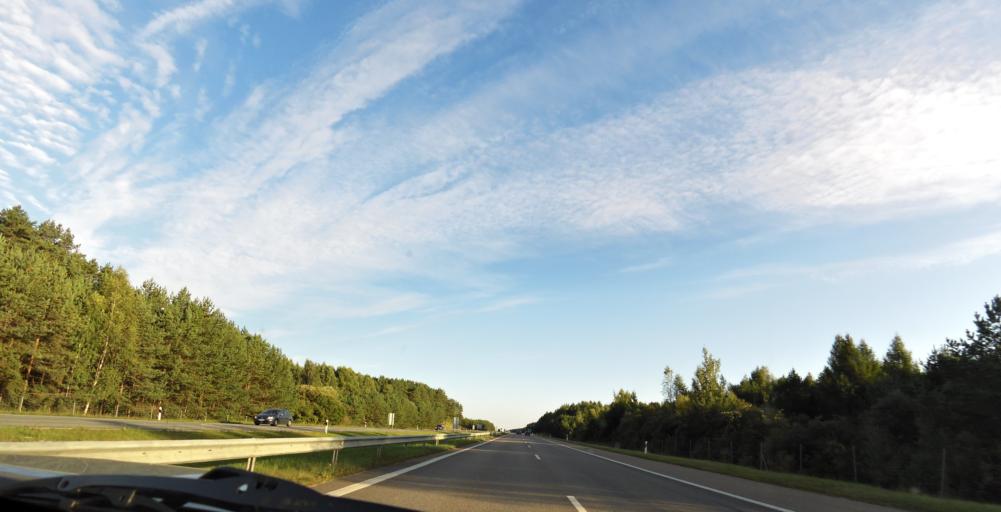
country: LT
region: Vilnius County
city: Ukmerge
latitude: 55.2592
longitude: 24.8150
